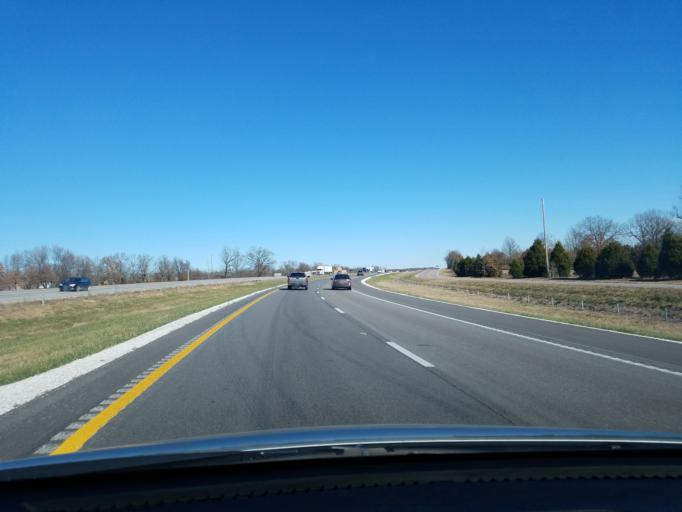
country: US
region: Missouri
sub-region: Greene County
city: Strafford
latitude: 37.2829
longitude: -93.0427
